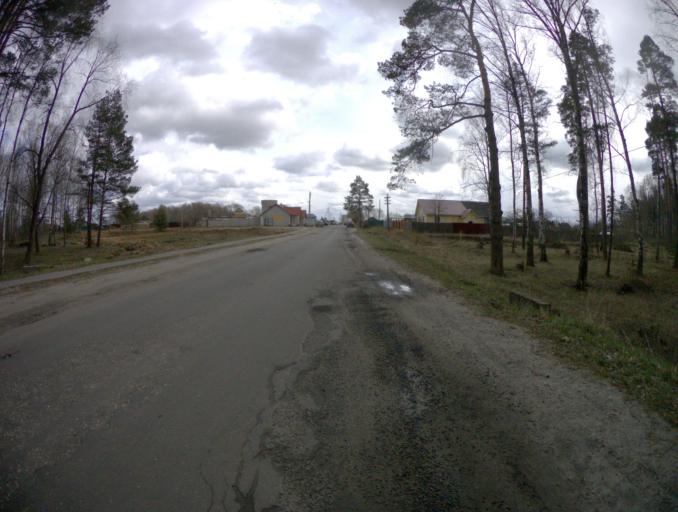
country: RU
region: Vladimir
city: Sudogda
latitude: 56.0704
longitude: 40.7931
